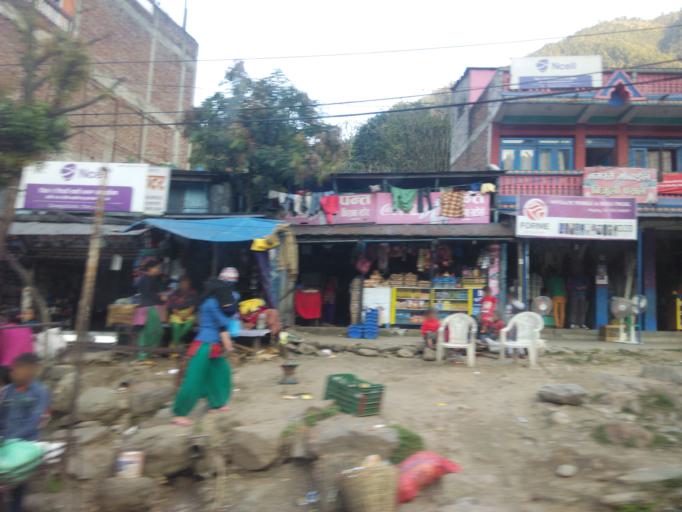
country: NP
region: Central Region
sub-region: Narayani Zone
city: Bharatpur
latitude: 27.8555
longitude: 84.5602
